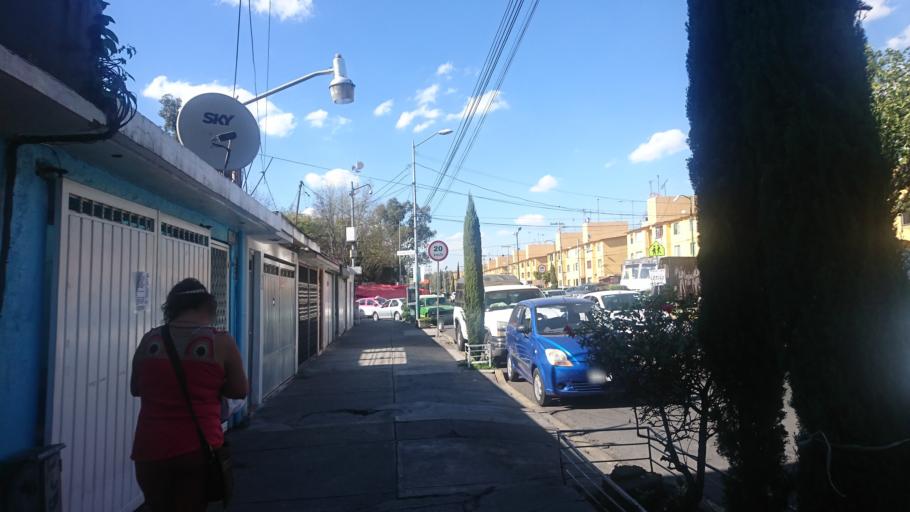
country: MX
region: Mexico City
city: Iztapalapa
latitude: 19.3251
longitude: -99.1067
